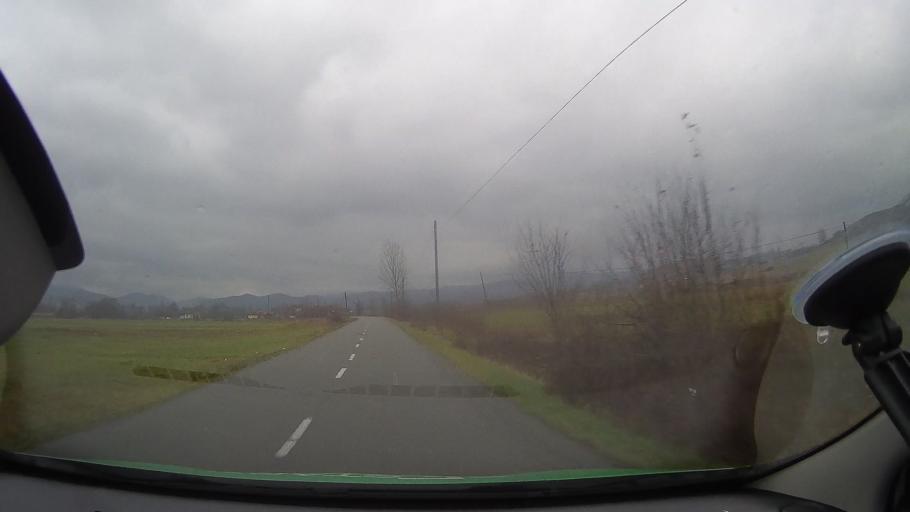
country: RO
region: Hunedoara
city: Vata de Jos
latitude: 46.1910
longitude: 22.6295
